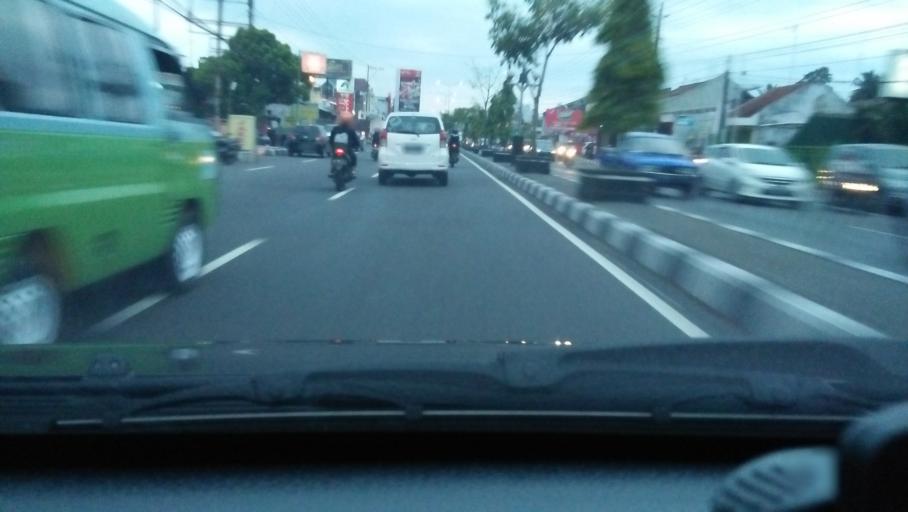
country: ID
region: Central Java
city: Mertoyudan
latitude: -7.5077
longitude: 110.2245
